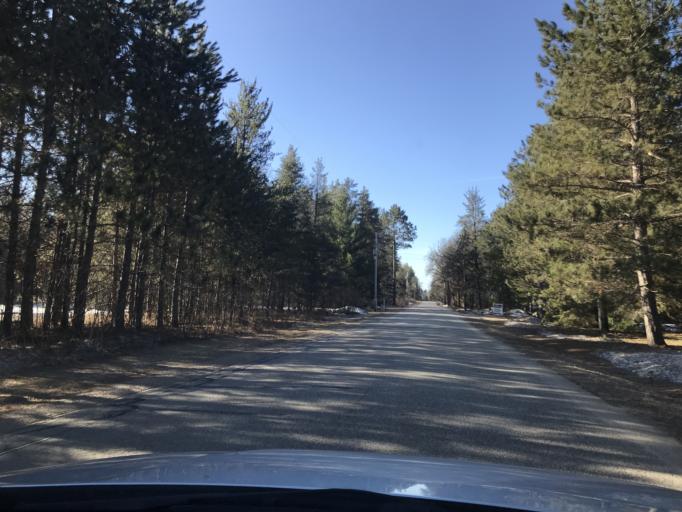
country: US
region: Michigan
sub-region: Dickinson County
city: Kingsford
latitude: 45.3941
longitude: -88.1612
